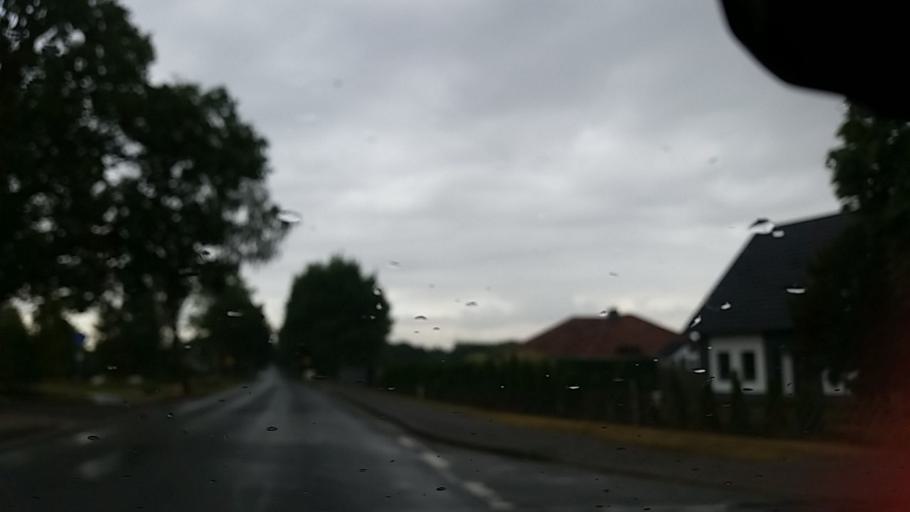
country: DE
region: Lower Saxony
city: Bokensdorf
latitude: 52.5438
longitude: 10.7126
